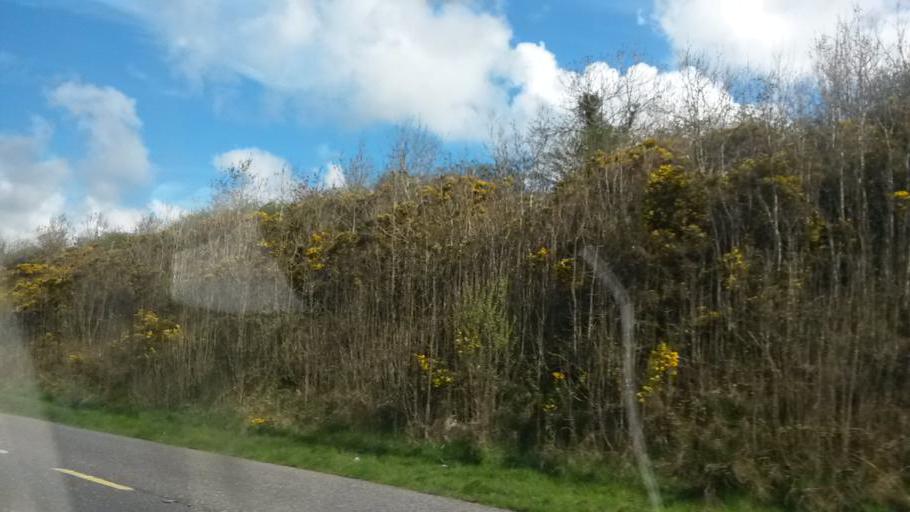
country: IE
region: Ulster
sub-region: An Cabhan
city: Virginia
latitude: 53.8688
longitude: -7.1181
